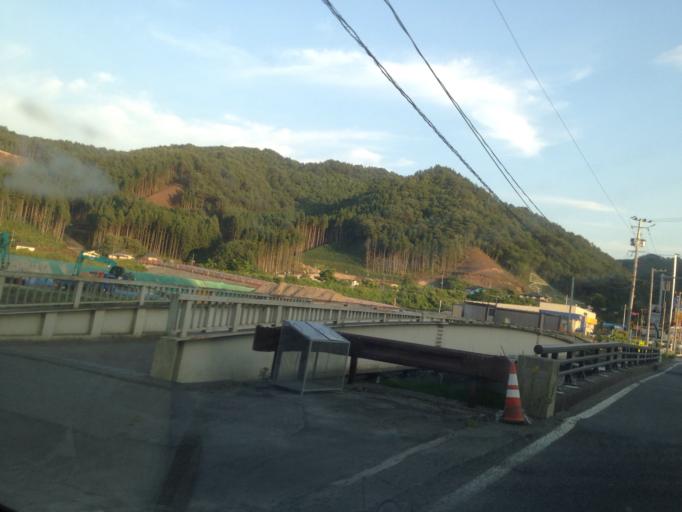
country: JP
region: Iwate
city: Otsuchi
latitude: 39.3236
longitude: 141.8846
